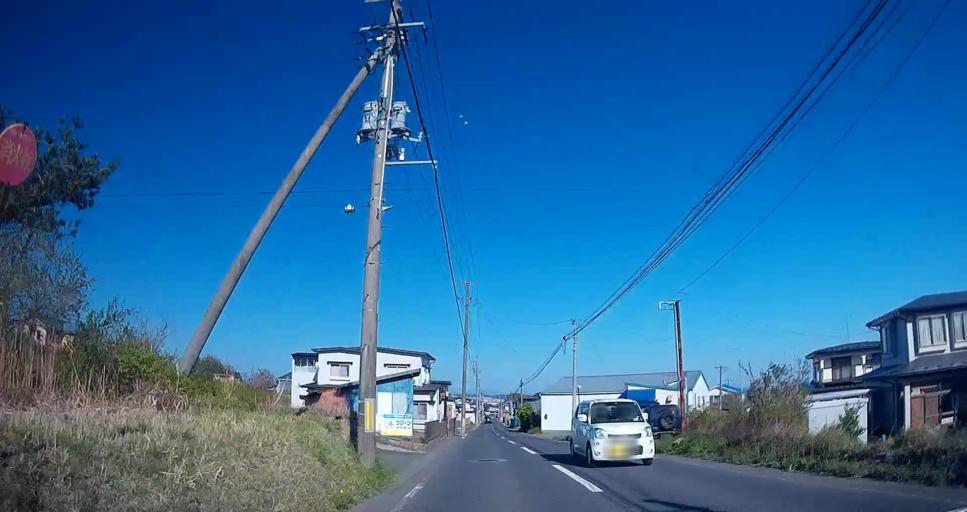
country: JP
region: Aomori
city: Hachinohe
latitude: 40.5233
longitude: 141.5568
